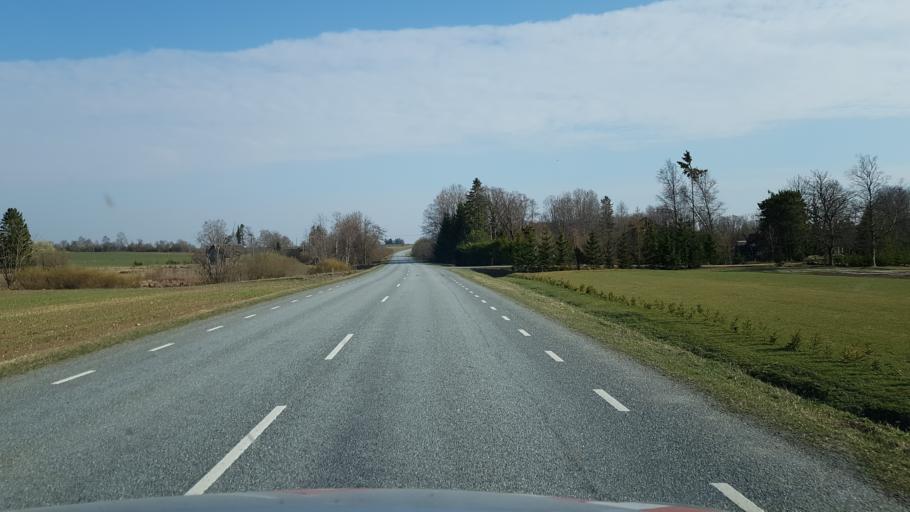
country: EE
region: Laeaene-Virumaa
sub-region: Kadrina vald
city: Kadrina
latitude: 59.3700
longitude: 26.1024
